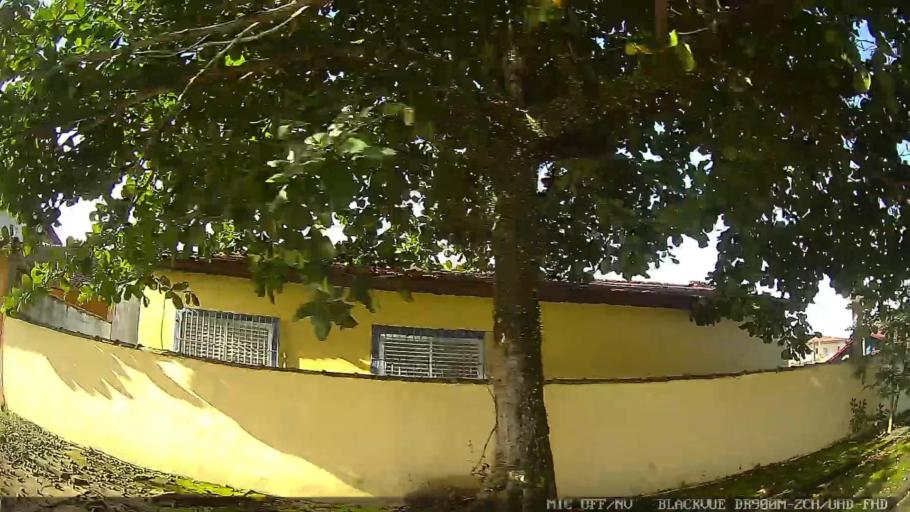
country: BR
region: Sao Paulo
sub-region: Itanhaem
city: Itanhaem
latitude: -24.1553
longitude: -46.7359
